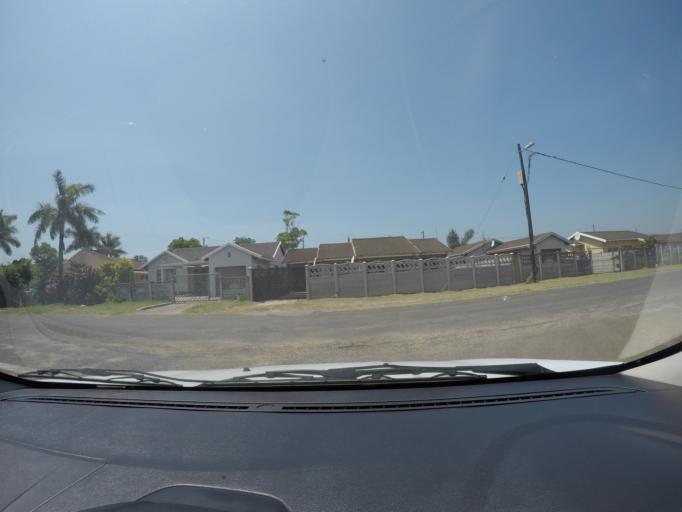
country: ZA
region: KwaZulu-Natal
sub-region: uThungulu District Municipality
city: eSikhawini
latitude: -28.8710
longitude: 31.9225
